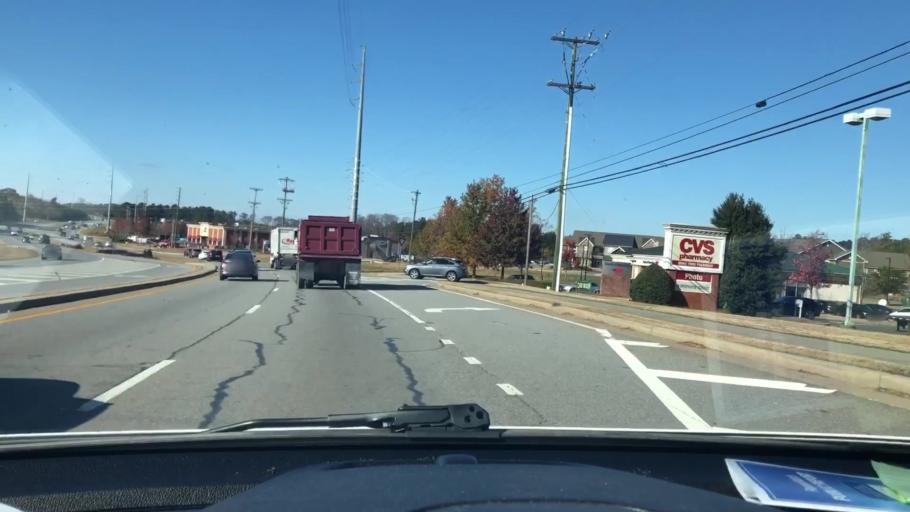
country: US
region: Georgia
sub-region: Fulton County
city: Johns Creek
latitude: 34.0849
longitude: -84.1618
